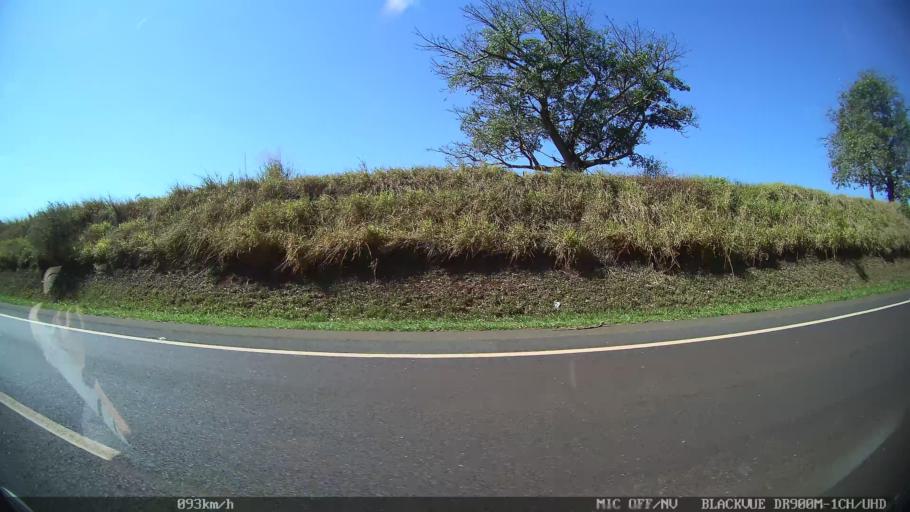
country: BR
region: Sao Paulo
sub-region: Batatais
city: Batatais
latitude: -20.7589
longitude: -47.5319
